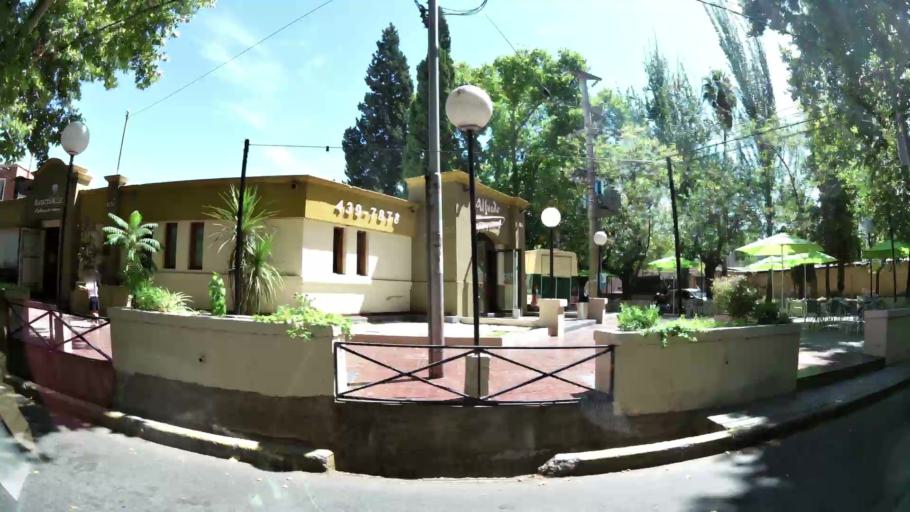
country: AR
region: Mendoza
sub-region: Departamento de Godoy Cruz
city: Godoy Cruz
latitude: -32.9618
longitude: -68.8609
